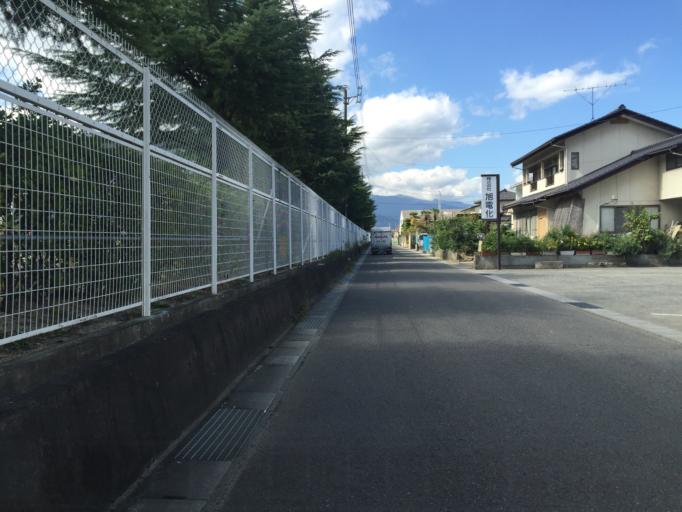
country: JP
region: Fukushima
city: Fukushima-shi
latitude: 37.7306
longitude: 140.4567
